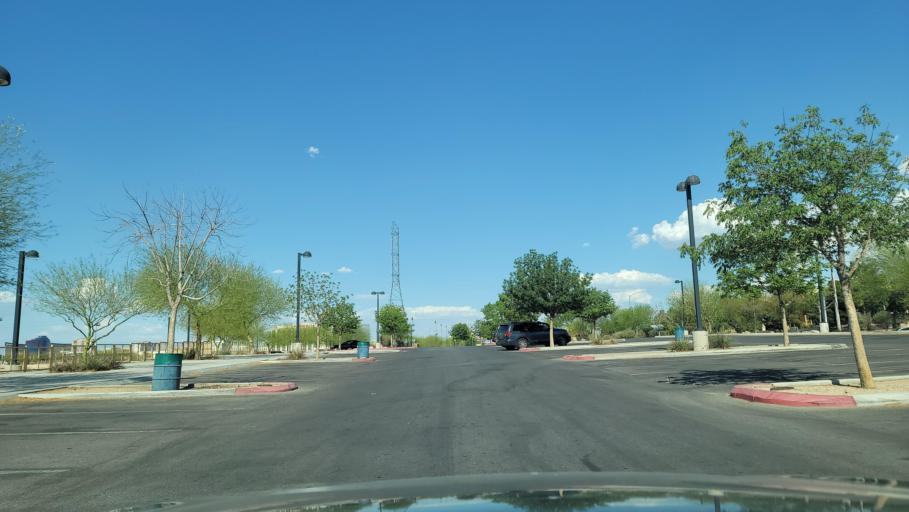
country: US
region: Nevada
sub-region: Clark County
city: Spring Valley
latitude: 36.1009
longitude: -115.2147
